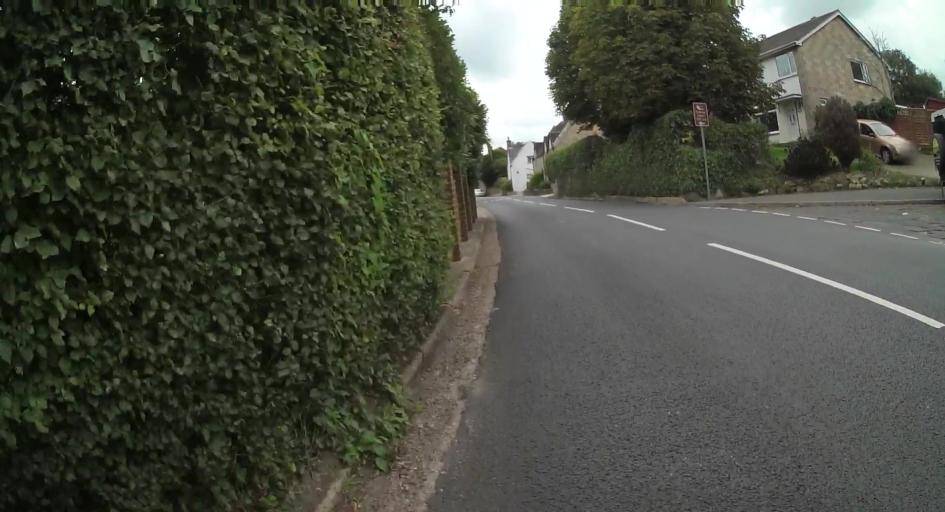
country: GB
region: England
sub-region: Isle of Wight
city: Niton
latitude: 50.6009
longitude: -1.2660
